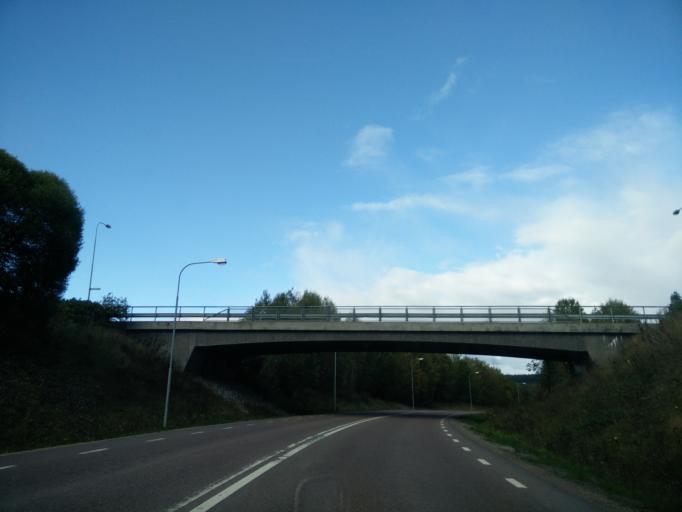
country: SE
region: Vaesternorrland
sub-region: Sundsvalls Kommun
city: Matfors
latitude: 62.3495
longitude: 17.0105
